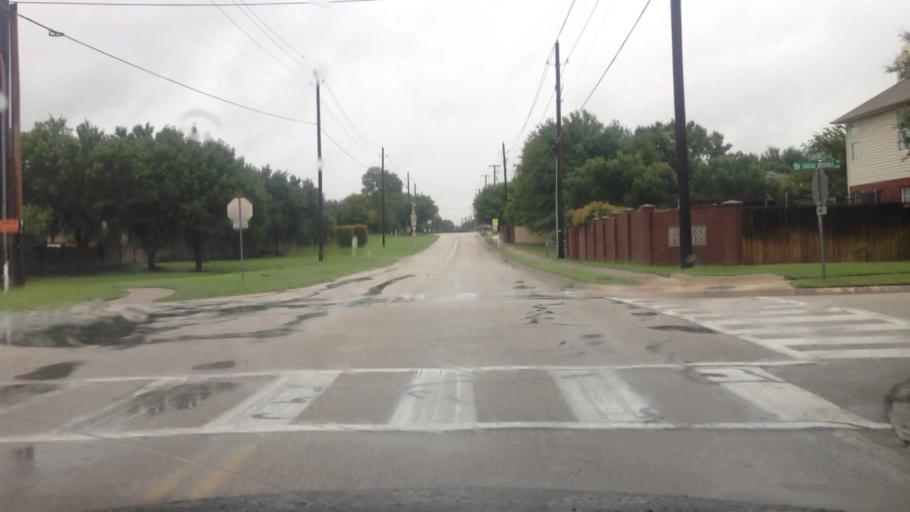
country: US
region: Texas
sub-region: Tarrant County
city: Keller
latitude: 32.9075
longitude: -97.2168
